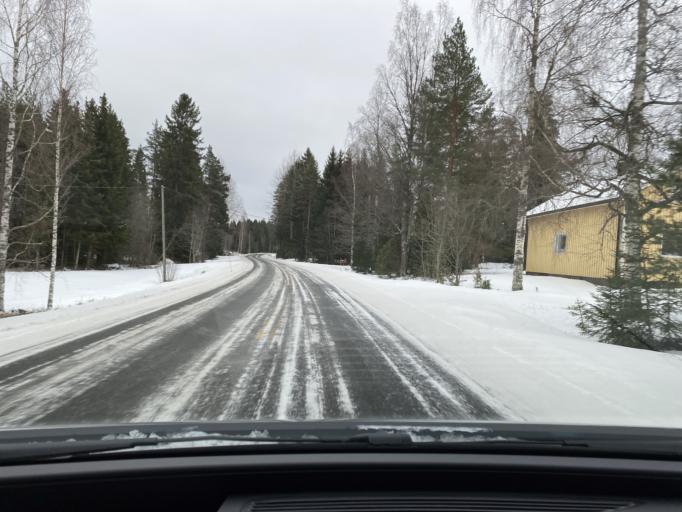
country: FI
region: Pirkanmaa
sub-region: Lounais-Pirkanmaa
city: Punkalaidun
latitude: 61.1892
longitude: 23.0397
